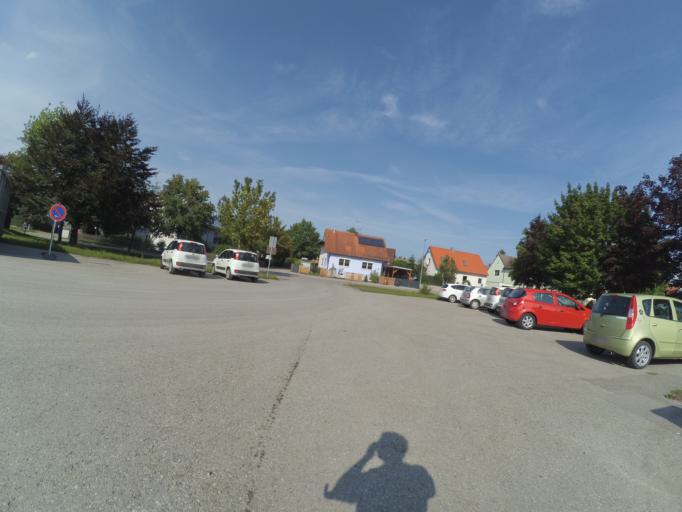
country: DE
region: Bavaria
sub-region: Swabia
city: Buchloe
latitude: 48.0446
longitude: 10.7247
